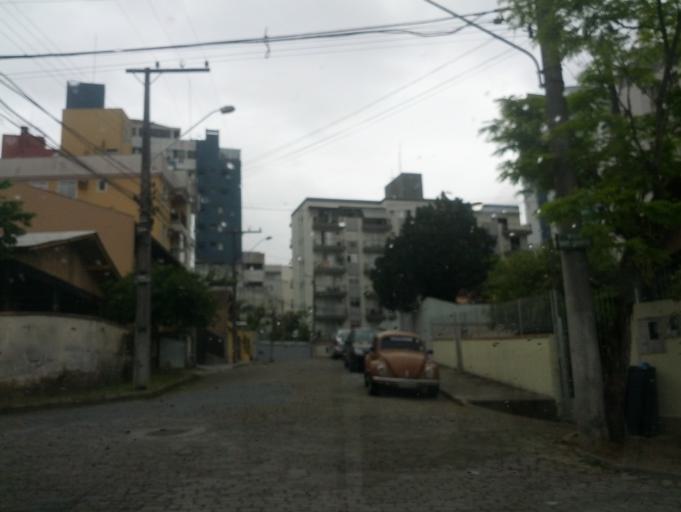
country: BR
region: Santa Catarina
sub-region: Blumenau
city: Blumenau
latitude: -26.9067
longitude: -49.0875
